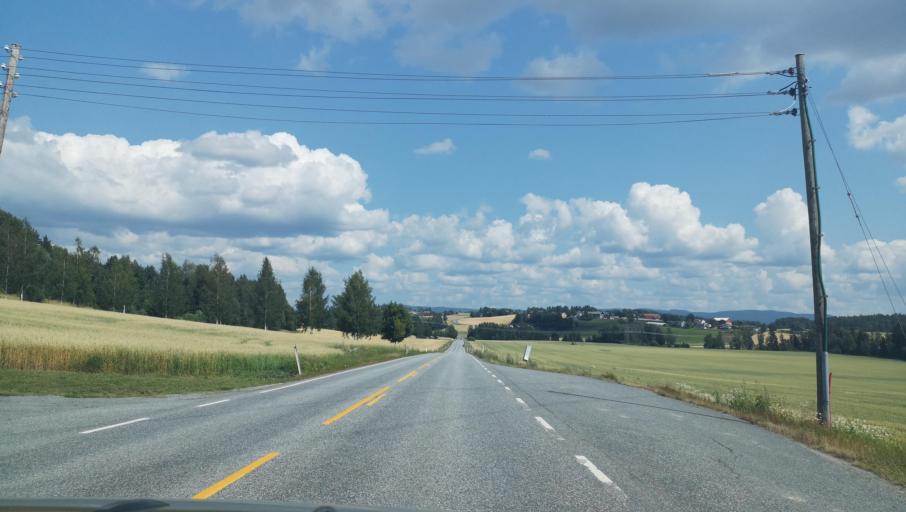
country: NO
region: Buskerud
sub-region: Ovre Eiker
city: Hokksund
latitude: 59.7185
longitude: 9.8244
